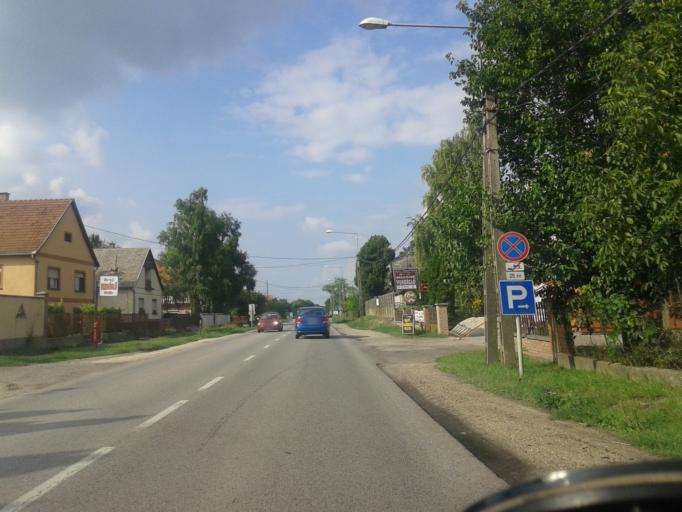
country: HU
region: Bacs-Kiskun
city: Solt
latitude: 46.8095
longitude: 19.0052
